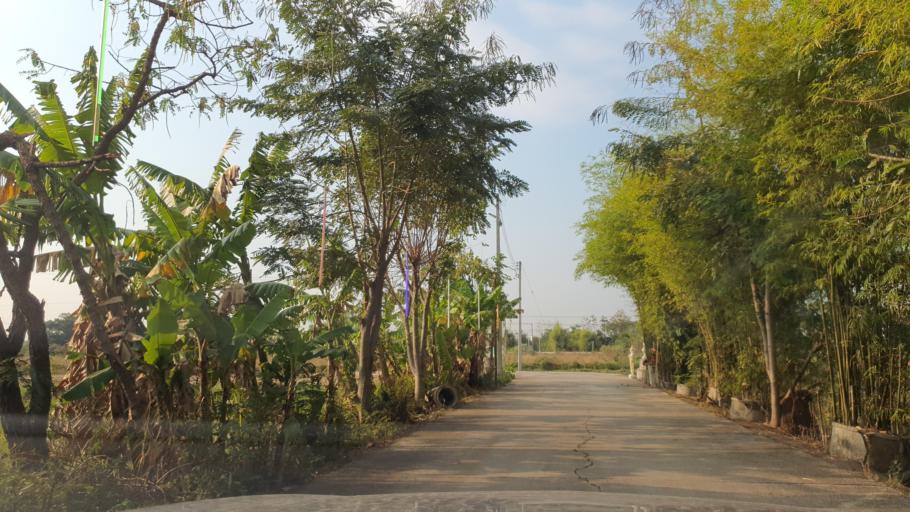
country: TH
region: Chiang Mai
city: San Kamphaeng
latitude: 18.7313
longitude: 99.0987
